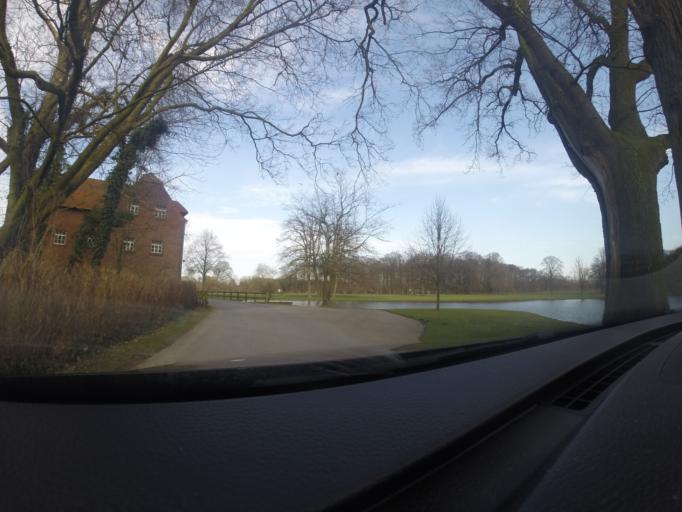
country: DE
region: North Rhine-Westphalia
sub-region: Regierungsbezirk Munster
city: Billerbeck
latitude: 52.0216
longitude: 7.2612
